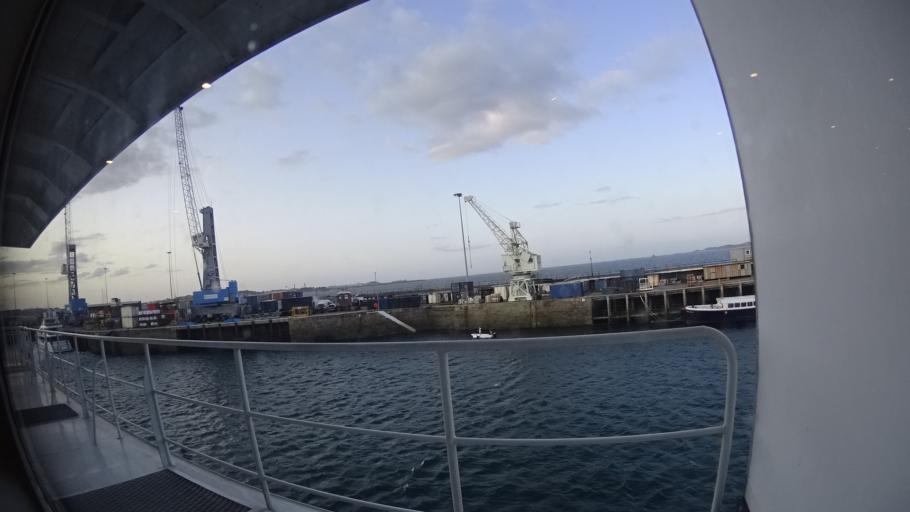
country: GG
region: St Peter Port
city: Saint Peter Port
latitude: 49.4568
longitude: -2.5277
